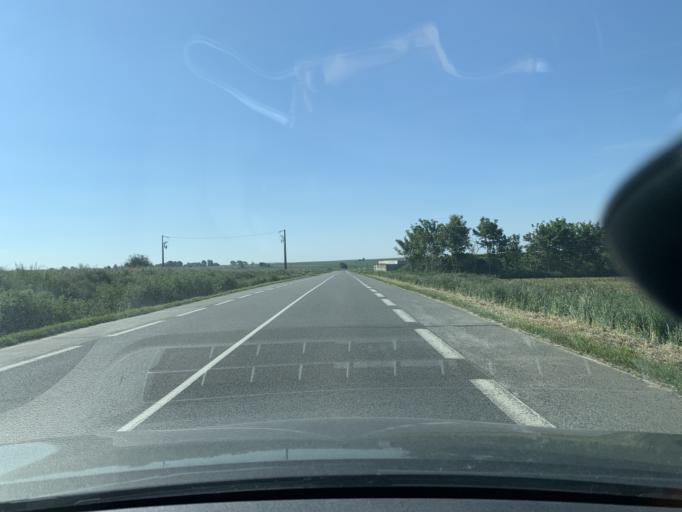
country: FR
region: Nord-Pas-de-Calais
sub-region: Departement du Nord
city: Cambrai
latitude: 50.1414
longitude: 3.2454
